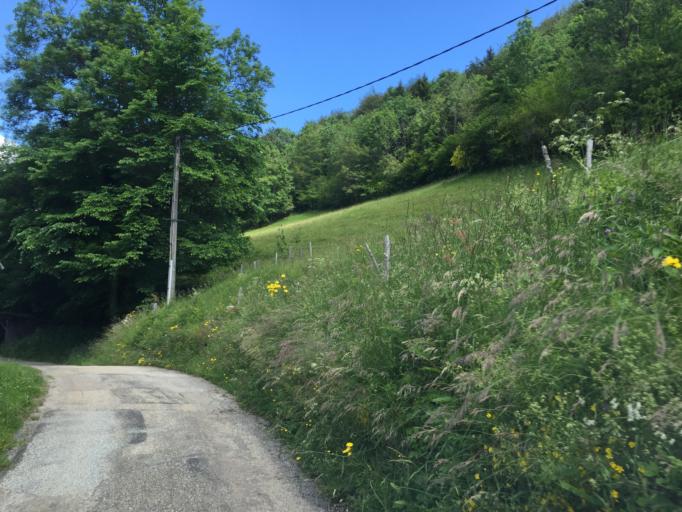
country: FR
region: Rhone-Alpes
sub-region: Departement de la Savoie
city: Vimines
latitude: 45.4787
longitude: 5.8920
